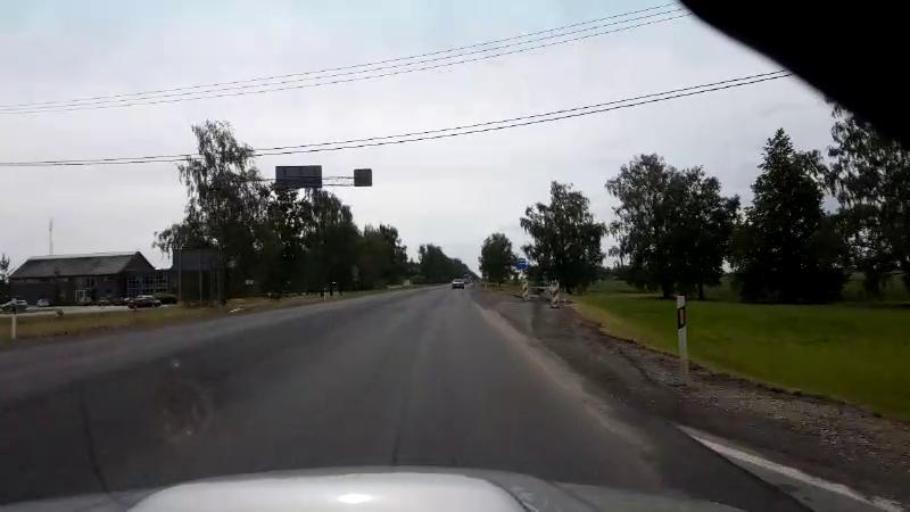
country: LV
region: Bauskas Rajons
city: Bauska
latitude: 56.3588
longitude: 24.2837
